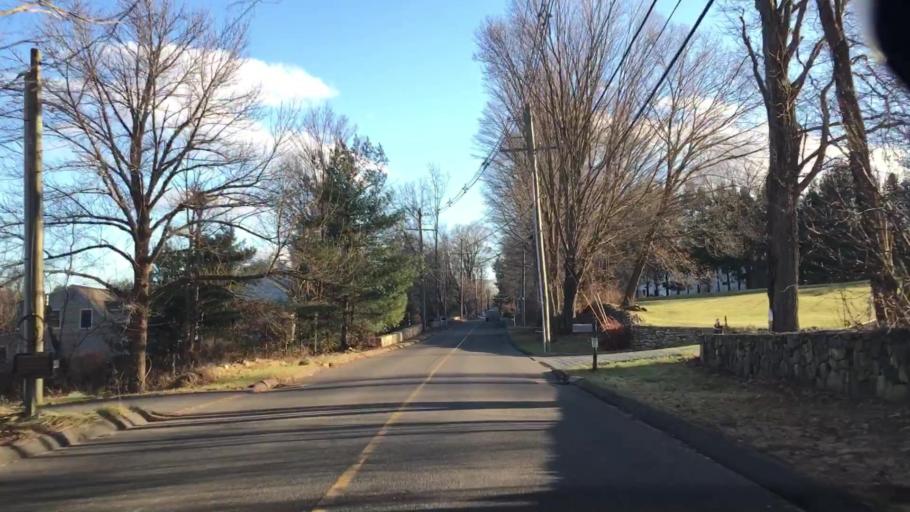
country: US
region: Connecticut
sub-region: Fairfield County
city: Newtown
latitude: 41.4220
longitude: -73.3072
